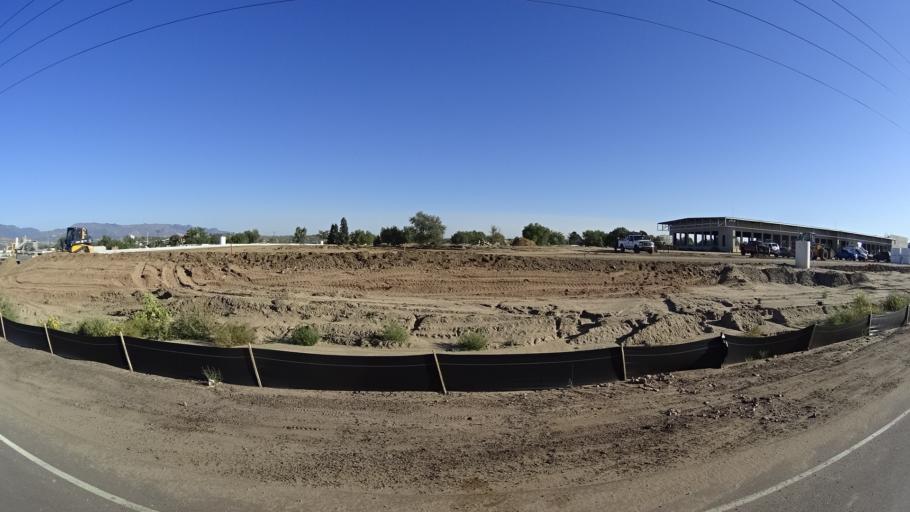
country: US
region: Colorado
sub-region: El Paso County
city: Stratmoor
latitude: 38.7817
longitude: -104.7611
